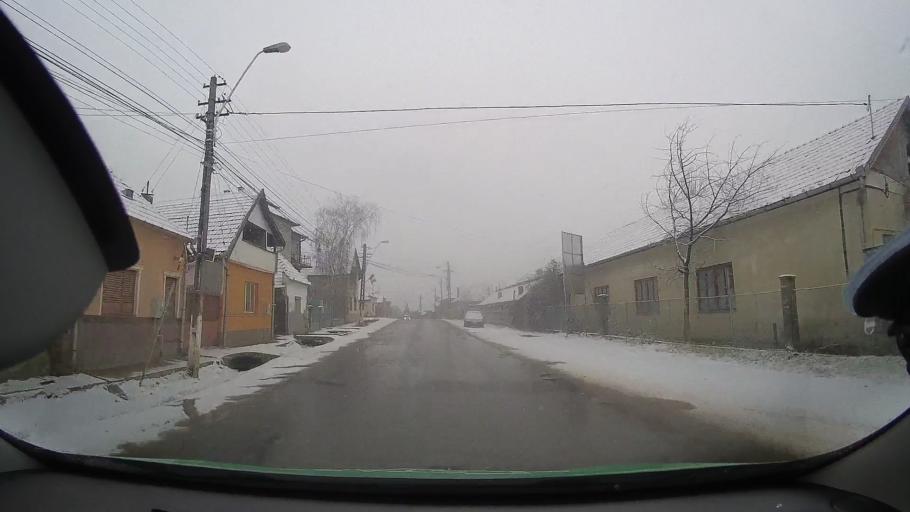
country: RO
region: Alba
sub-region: Municipiul Aiud
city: Aiudul de Sus
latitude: 46.3115
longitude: 23.7018
